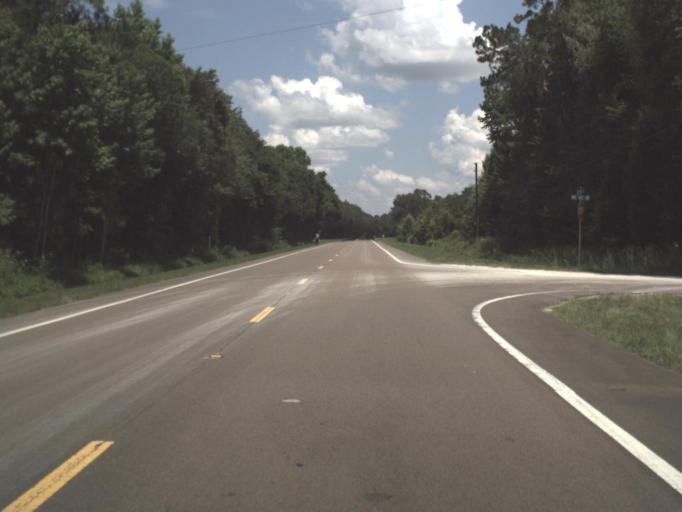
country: US
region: Florida
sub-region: Alachua County
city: Alachua
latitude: 29.7847
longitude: -82.3768
